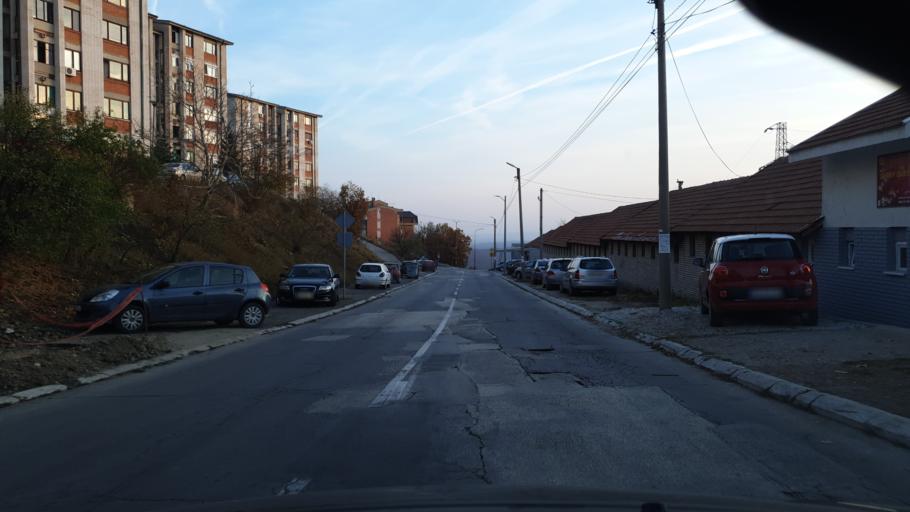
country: RS
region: Central Serbia
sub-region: Borski Okrug
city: Bor
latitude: 44.0567
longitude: 22.0952
